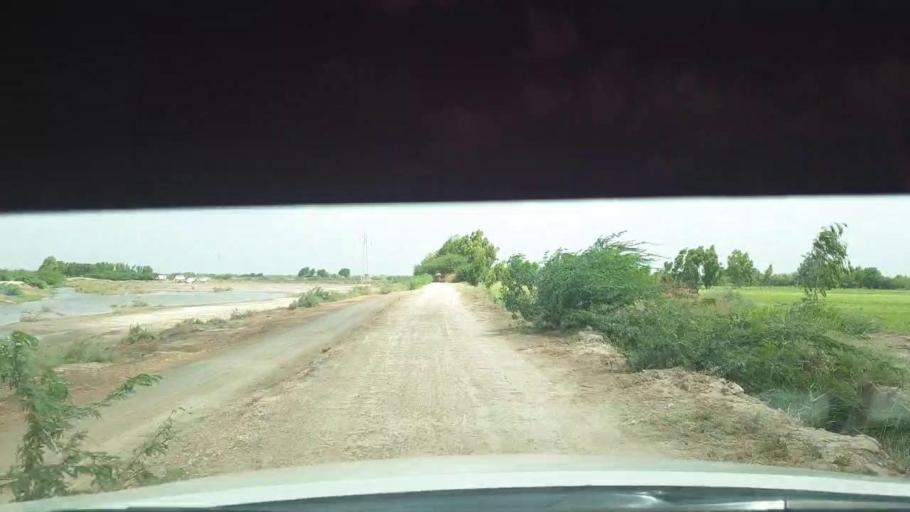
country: PK
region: Sindh
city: Kadhan
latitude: 24.4903
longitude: 68.9827
